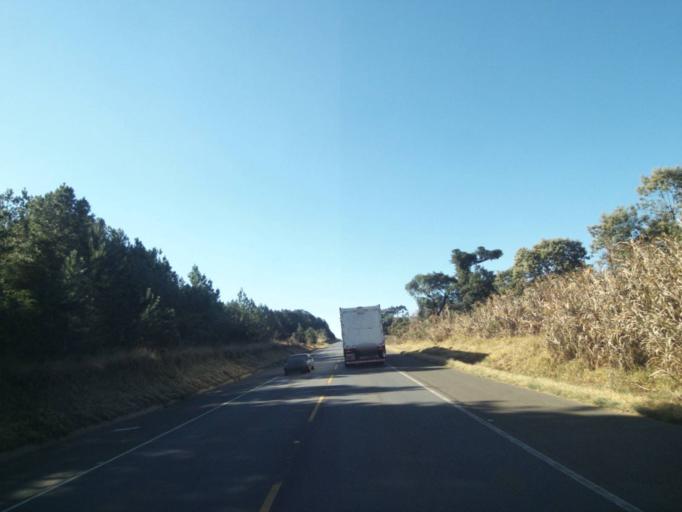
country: BR
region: Parana
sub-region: Tibagi
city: Tibagi
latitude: -24.5469
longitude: -50.4514
